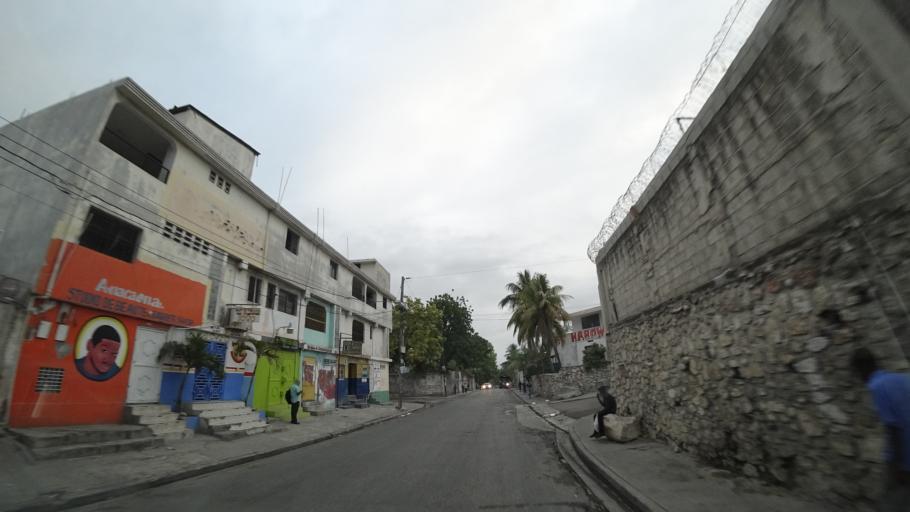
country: HT
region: Ouest
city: Delmas 73
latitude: 18.5510
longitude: -72.3063
